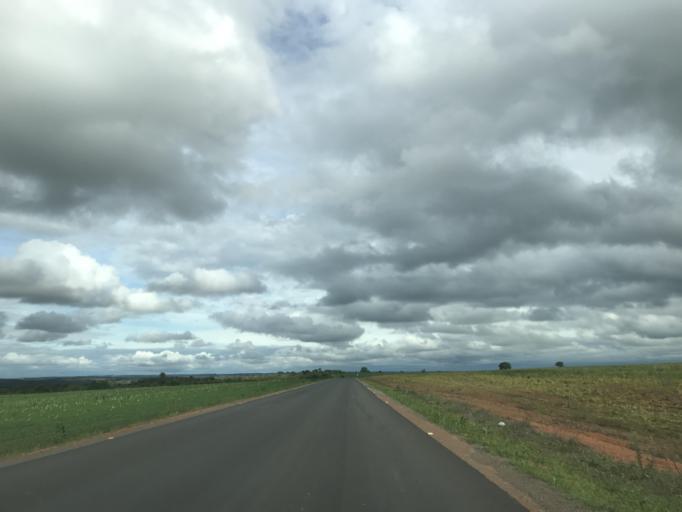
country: BR
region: Goias
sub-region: Vianopolis
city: Vianopolis
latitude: -16.9670
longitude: -48.6119
